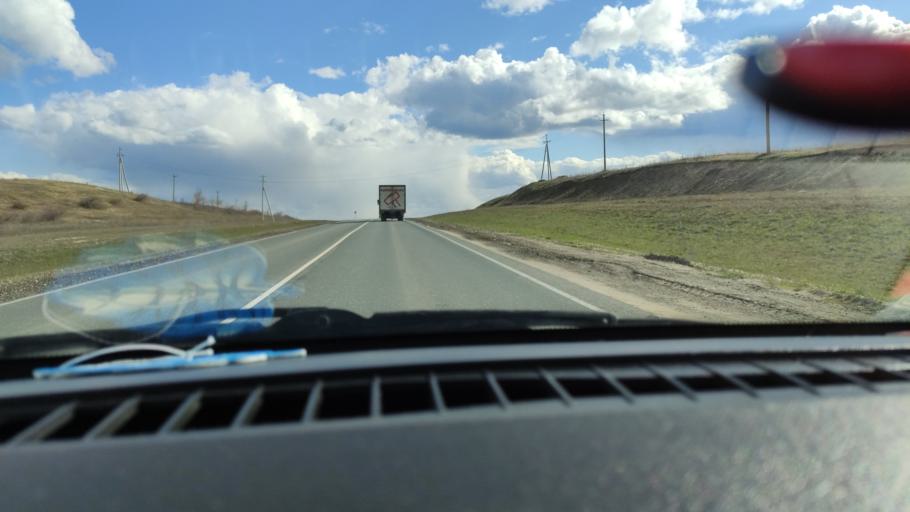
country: RU
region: Saratov
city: Alekseyevka
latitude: 52.3199
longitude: 47.9222
